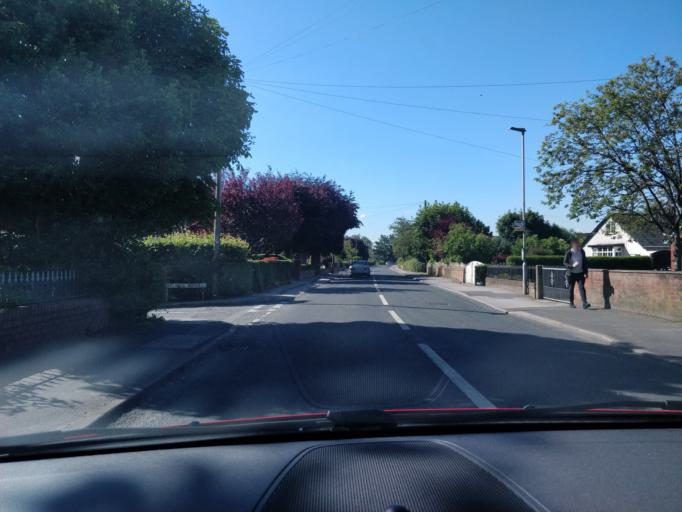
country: GB
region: England
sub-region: Lancashire
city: Tarleton
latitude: 53.6832
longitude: -2.8307
